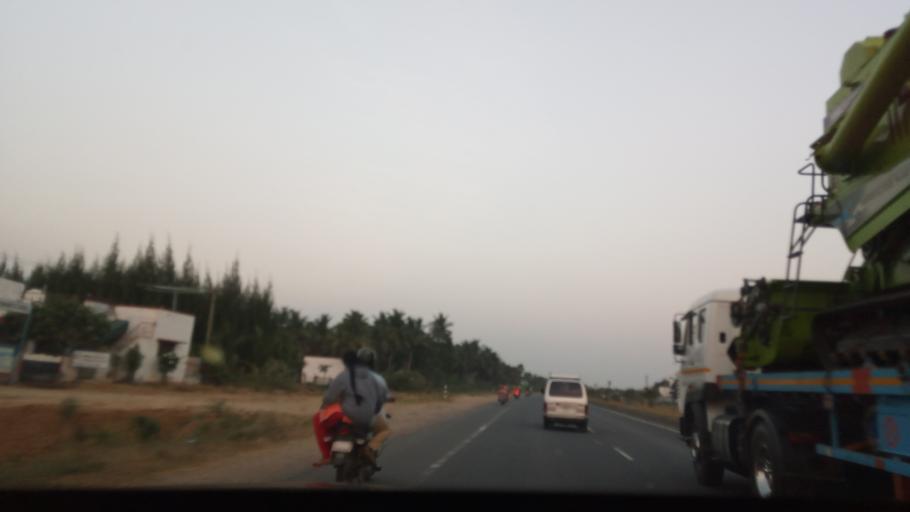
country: IN
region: Tamil Nadu
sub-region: Salem
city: Salem
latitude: 11.6650
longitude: 78.2888
